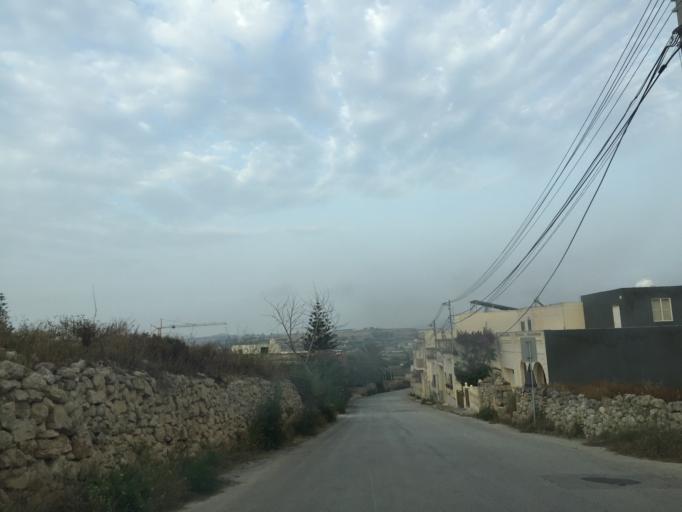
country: MT
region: Saint Paul's Bay
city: San Pawl il-Bahar
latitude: 35.9387
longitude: 14.4077
